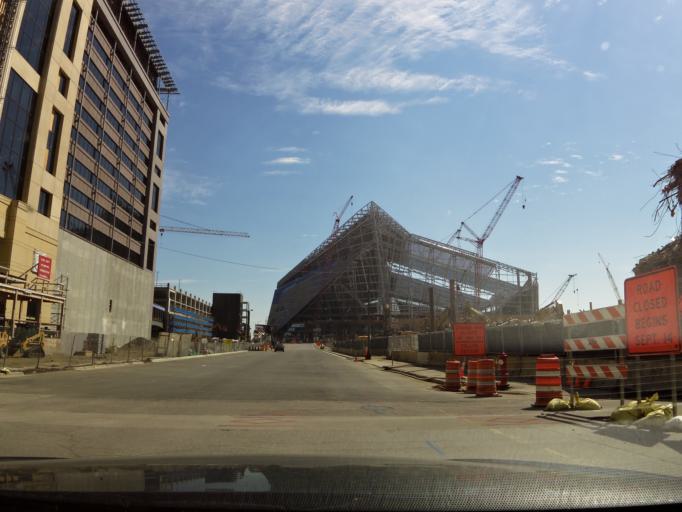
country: US
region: Minnesota
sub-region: Hennepin County
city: Minneapolis
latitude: 44.9763
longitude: -93.2617
